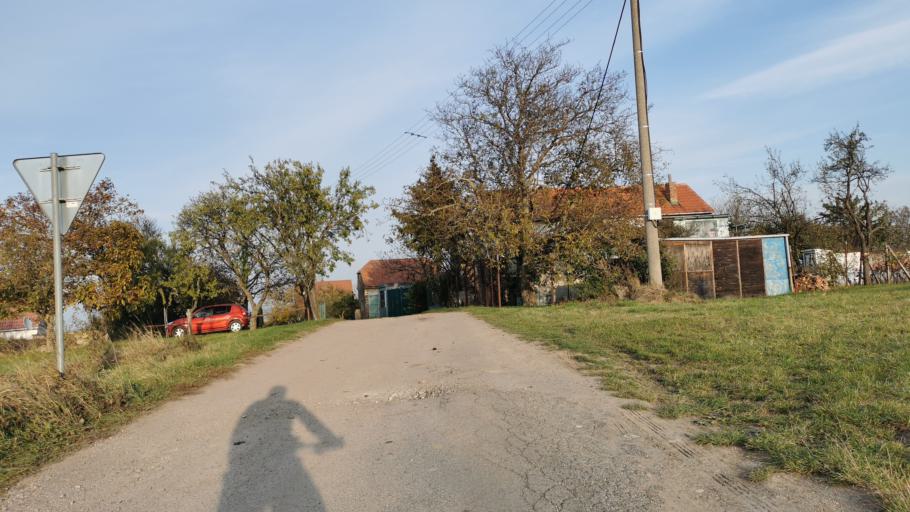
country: SK
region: Trnavsky
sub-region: Okres Skalica
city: Skalica
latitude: 48.8313
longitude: 17.2449
